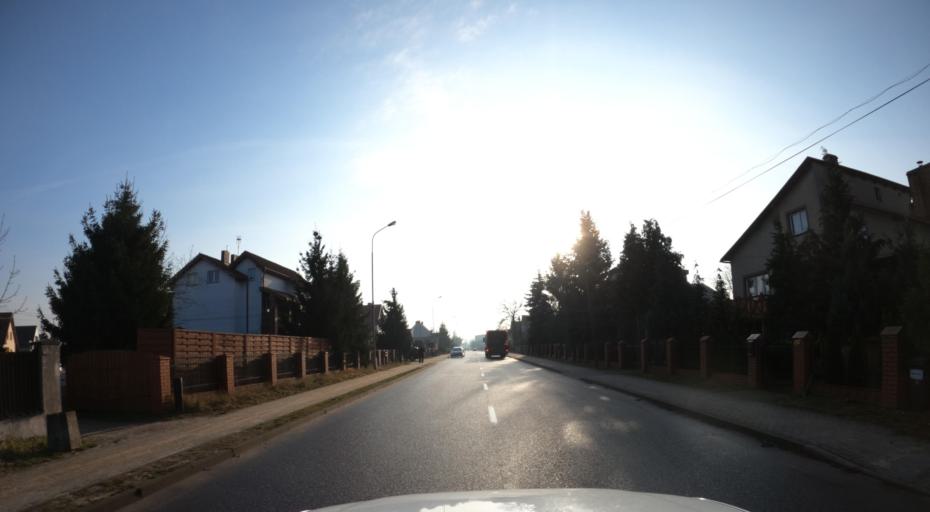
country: PL
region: Lubusz
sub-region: Powiat gorzowski
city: Kostrzyn nad Odra
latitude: 52.6040
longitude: 14.6357
